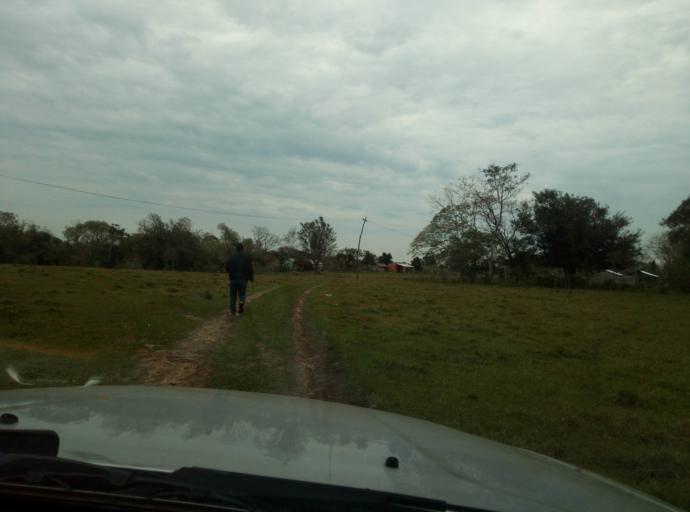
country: PY
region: Caaguazu
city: Carayao
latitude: -25.1616
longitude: -56.3336
